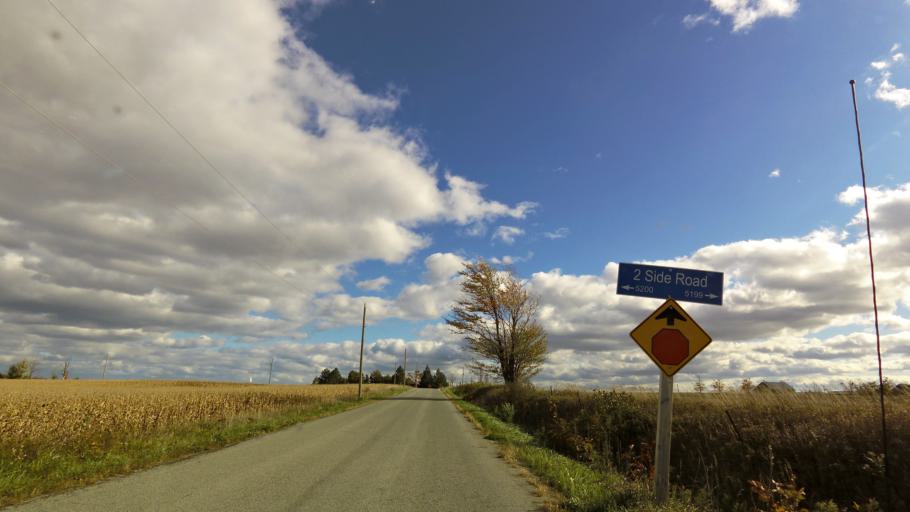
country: CA
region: Ontario
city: Burlington
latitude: 43.4339
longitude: -79.8310
